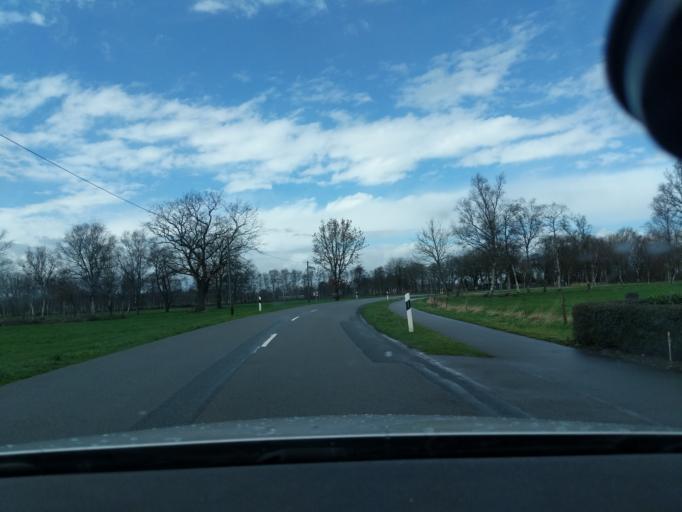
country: DE
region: Lower Saxony
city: Engelschoff
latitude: 53.6810
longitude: 9.3485
